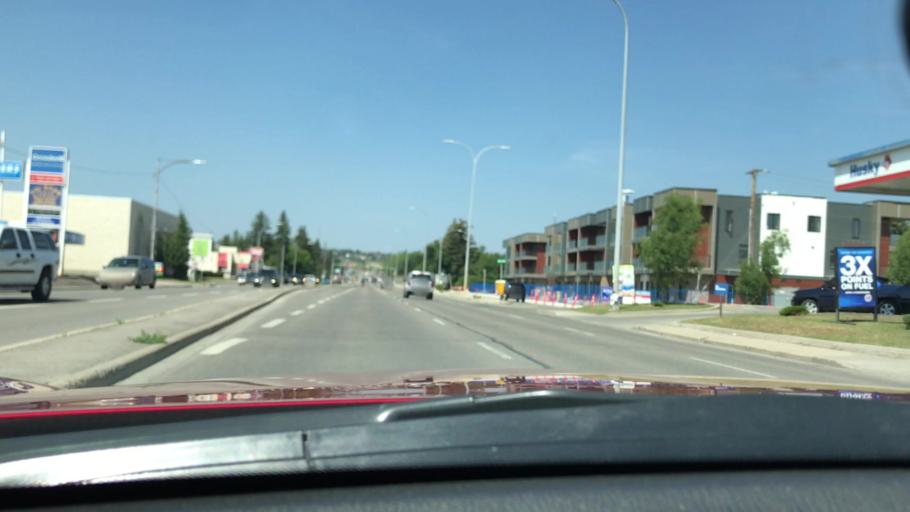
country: CA
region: Alberta
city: Calgary
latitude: 51.0457
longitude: -114.1428
